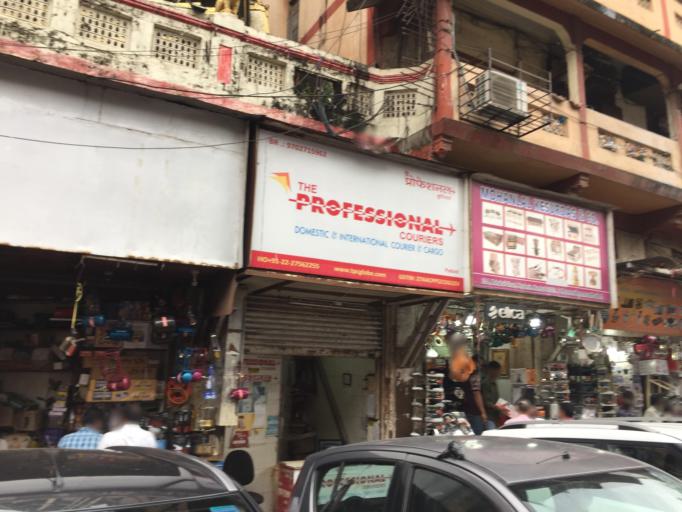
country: IN
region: Maharashtra
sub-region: Mumbai Suburban
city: Mumbai
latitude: 18.9537
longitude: 72.8313
